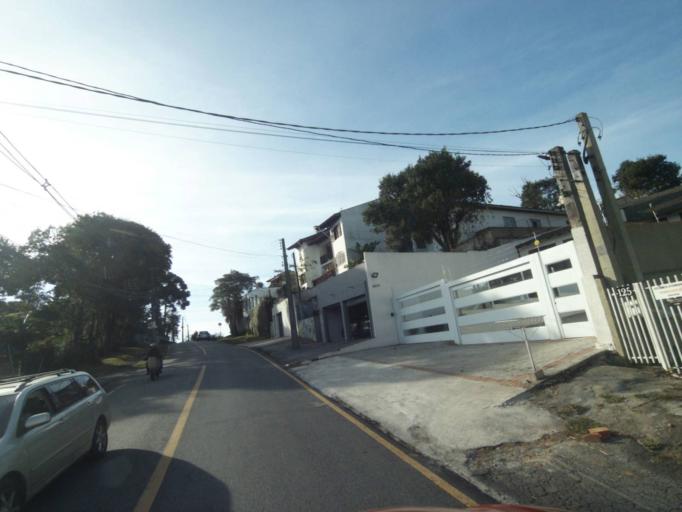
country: BR
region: Parana
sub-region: Curitiba
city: Curitiba
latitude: -25.4327
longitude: -49.3072
